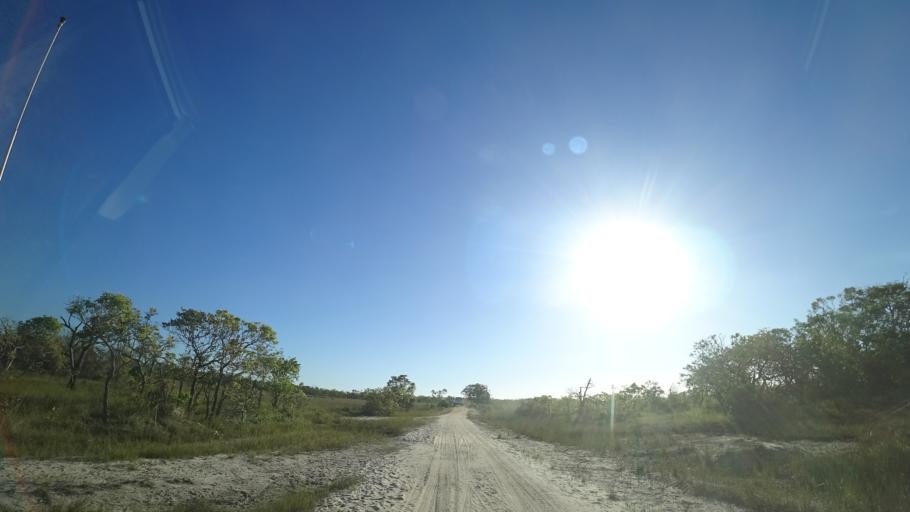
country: MZ
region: Sofala
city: Beira
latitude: -19.5760
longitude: 35.2039
